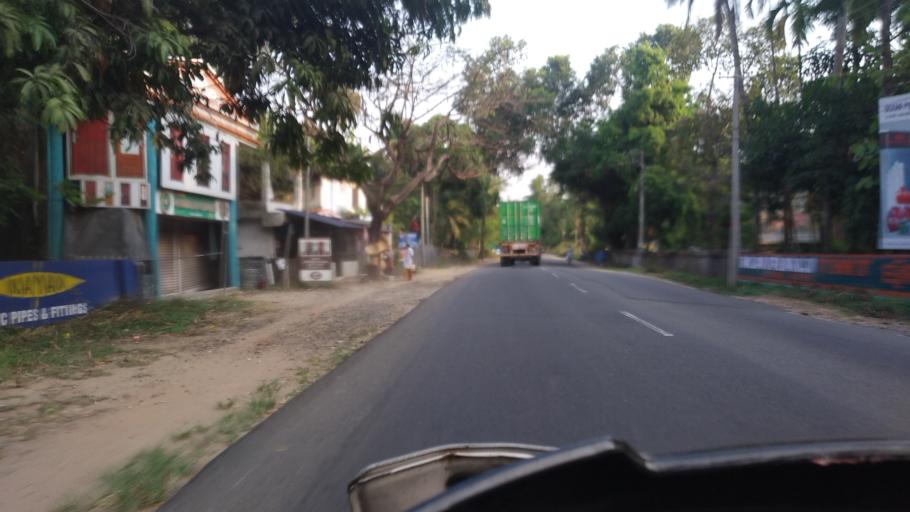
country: IN
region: Kerala
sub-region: Thrissur District
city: Thanniyam
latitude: 10.3509
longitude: 76.1318
